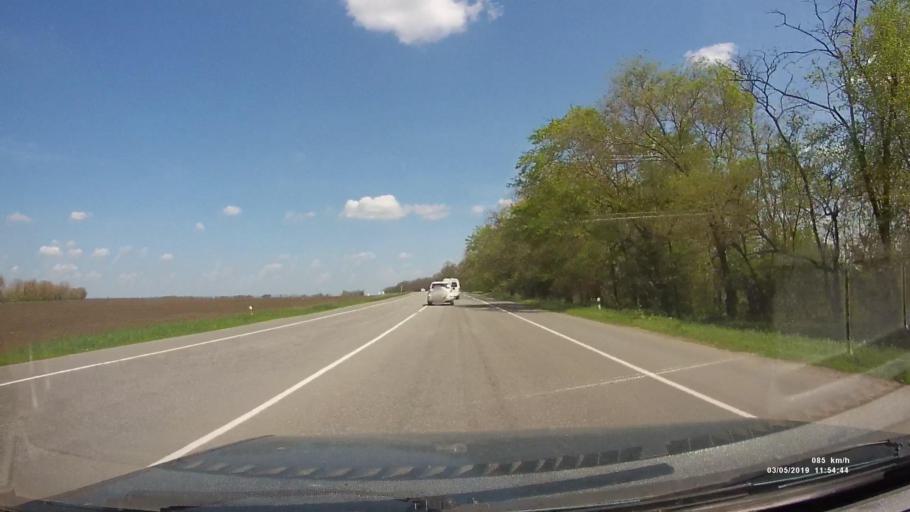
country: RU
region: Rostov
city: Bagayevskaya
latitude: 47.1727
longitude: 40.2841
